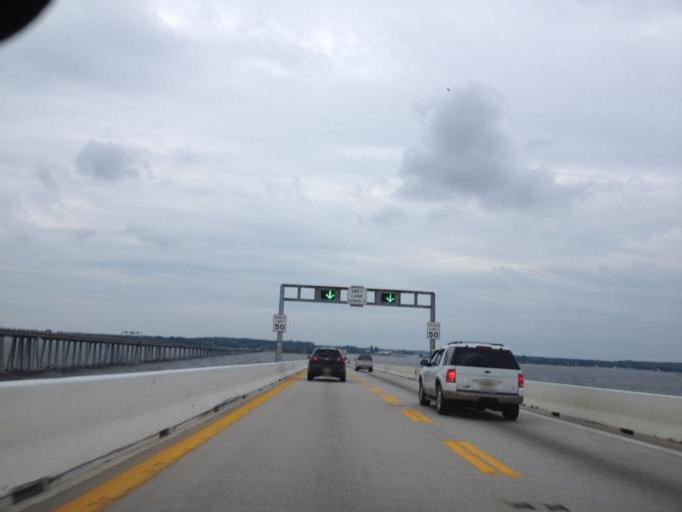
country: US
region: Maryland
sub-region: Queen Anne's County
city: Stevensville
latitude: 38.9867
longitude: -76.3542
